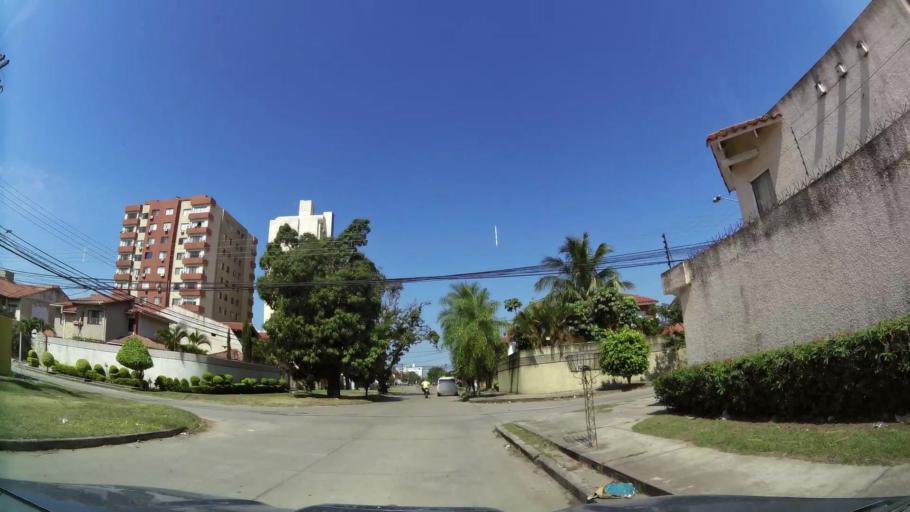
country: BO
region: Santa Cruz
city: Santa Cruz de la Sierra
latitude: -17.7432
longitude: -63.1686
